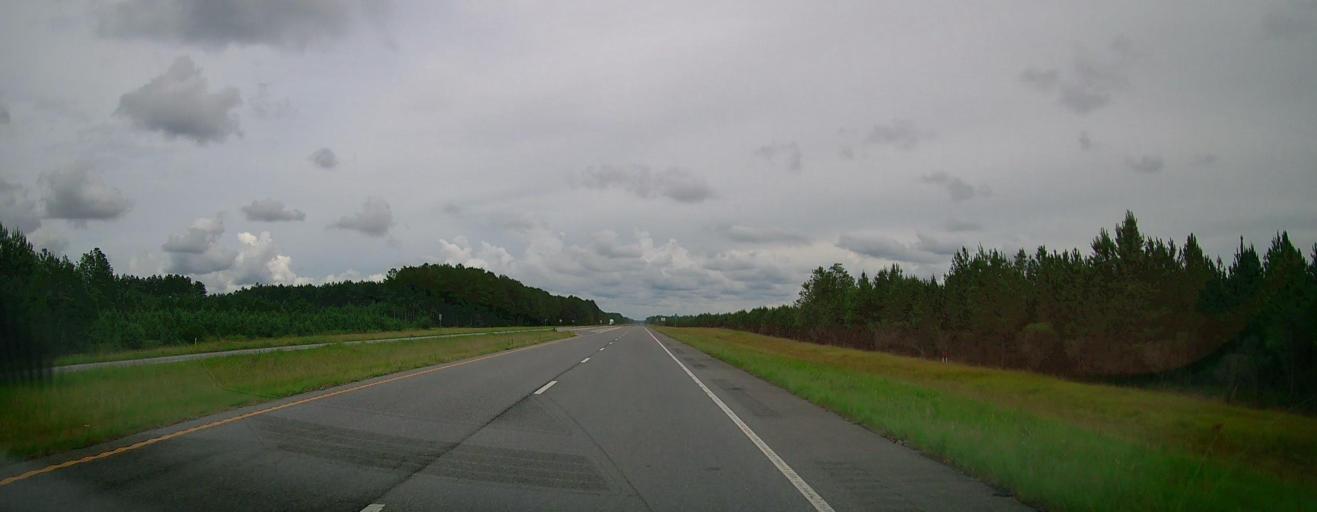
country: US
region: Georgia
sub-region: Appling County
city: Baxley
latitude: 31.7510
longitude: -82.2694
